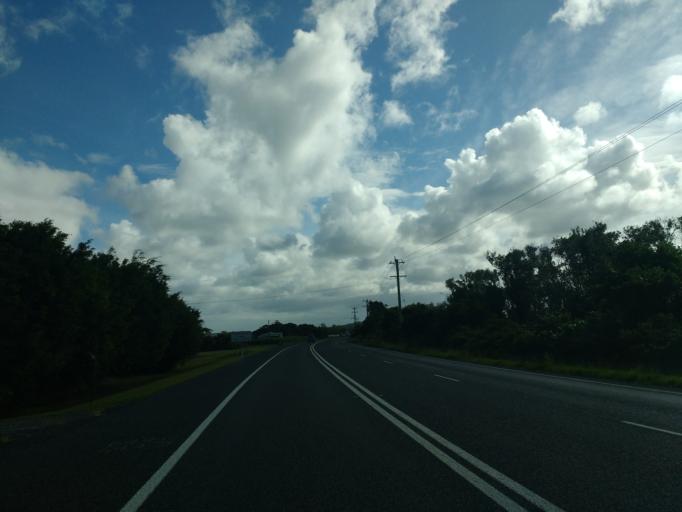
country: AU
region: New South Wales
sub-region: Richmond Valley
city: Evans Head
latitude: -28.9979
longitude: 153.4492
